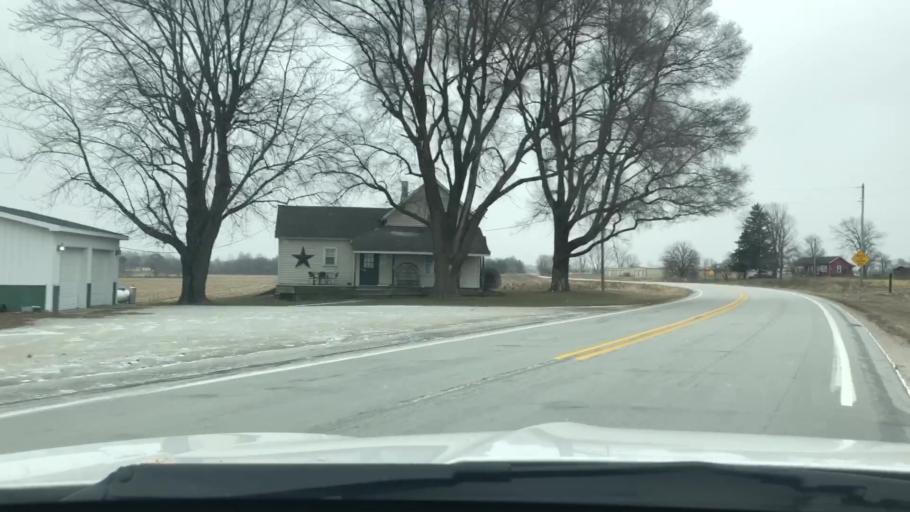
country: US
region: Indiana
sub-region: Fulton County
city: Akron
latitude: 41.0405
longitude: -86.0864
